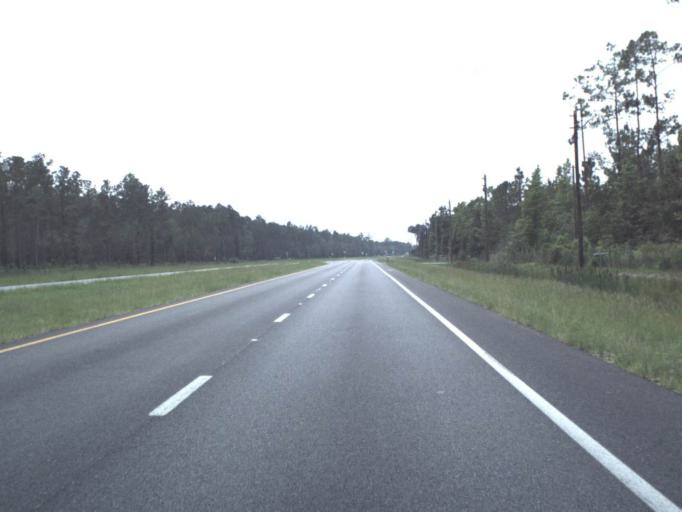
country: US
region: Florida
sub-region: Duval County
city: Baldwin
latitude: 30.4039
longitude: -81.9326
